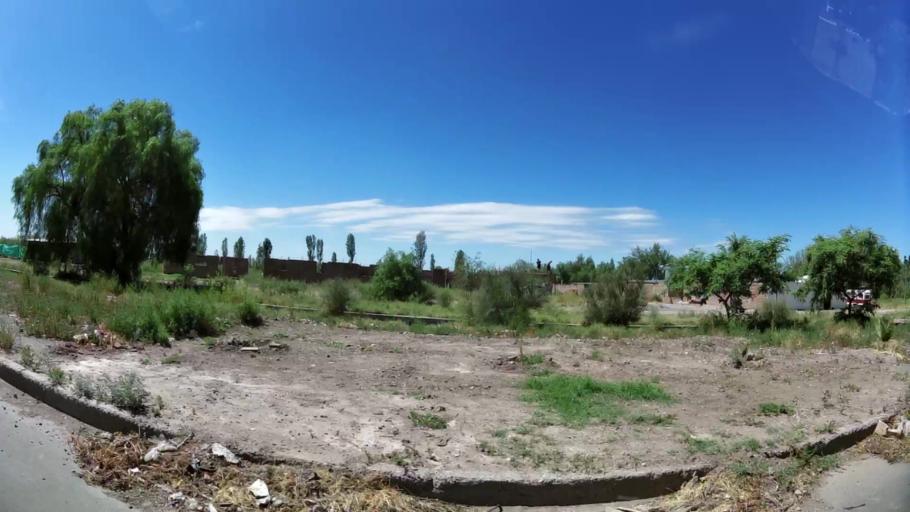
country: AR
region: Mendoza
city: Las Heras
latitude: -32.8390
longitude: -68.8627
